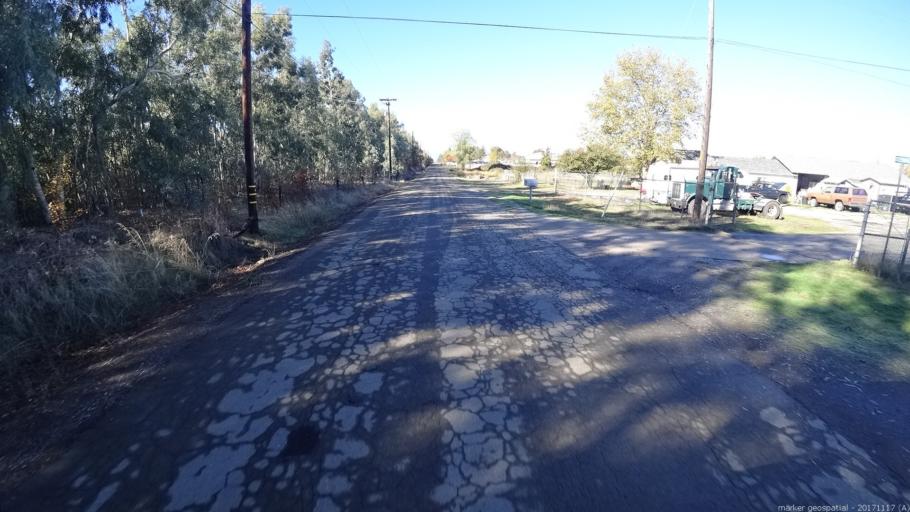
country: US
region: California
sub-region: Shasta County
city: Anderson
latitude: 40.4344
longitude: -122.2576
